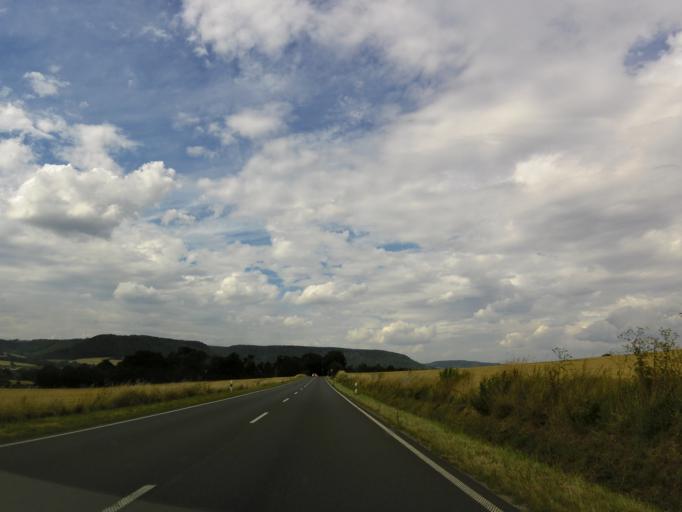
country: DE
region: Lower Saxony
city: Furstenberg
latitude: 51.7192
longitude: 9.3728
